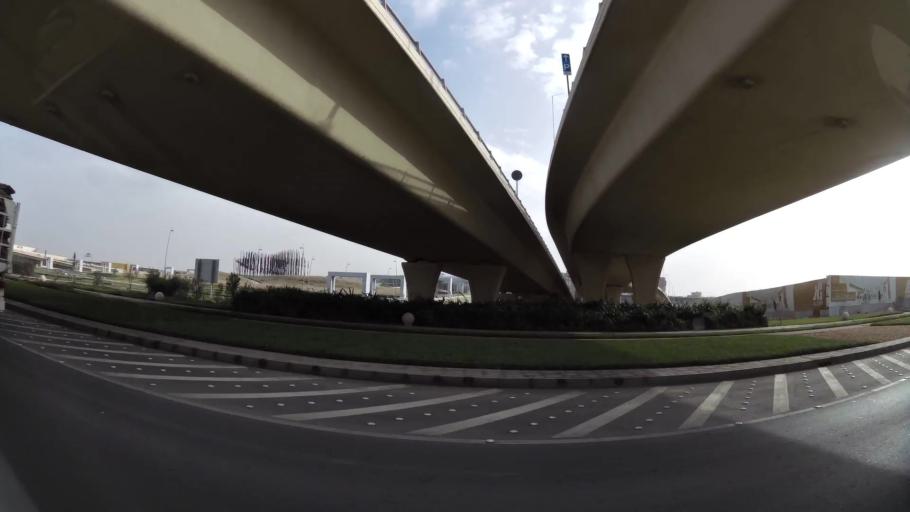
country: AE
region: Abu Dhabi
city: Abu Dhabi
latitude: 24.4941
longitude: 54.6091
